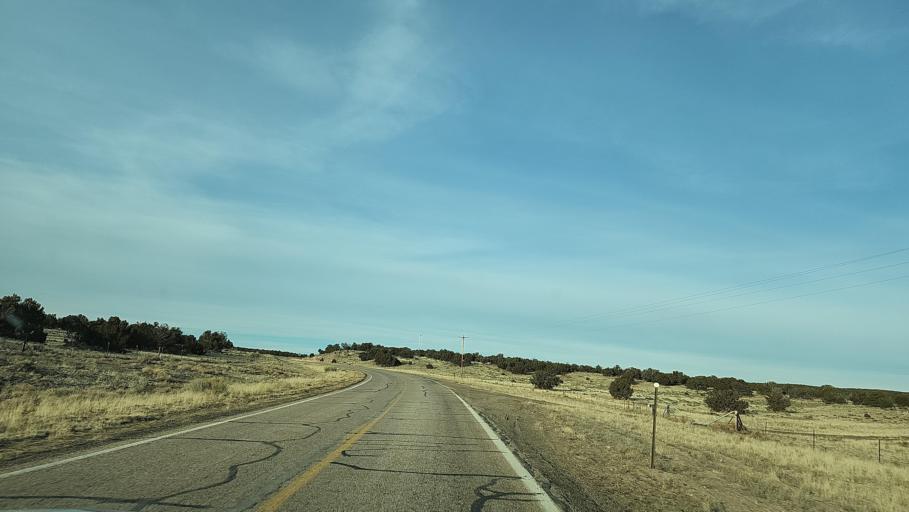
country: US
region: New Mexico
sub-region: Catron County
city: Reserve
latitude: 34.4052
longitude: -108.4378
